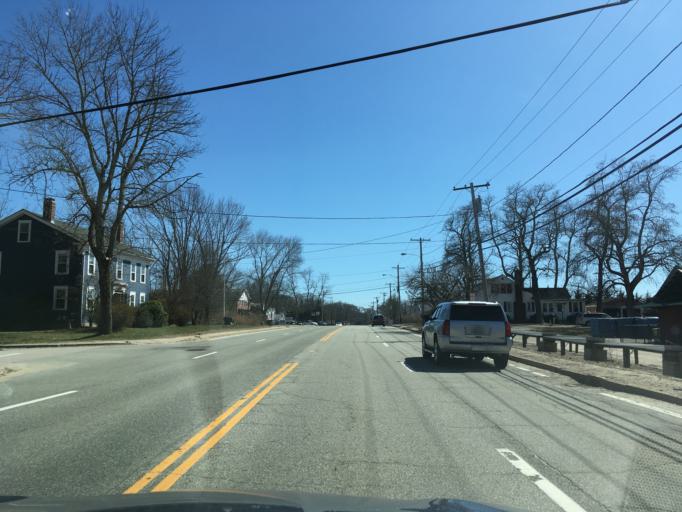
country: US
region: Rhode Island
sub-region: Kent County
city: East Greenwich
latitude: 41.6241
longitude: -71.4921
